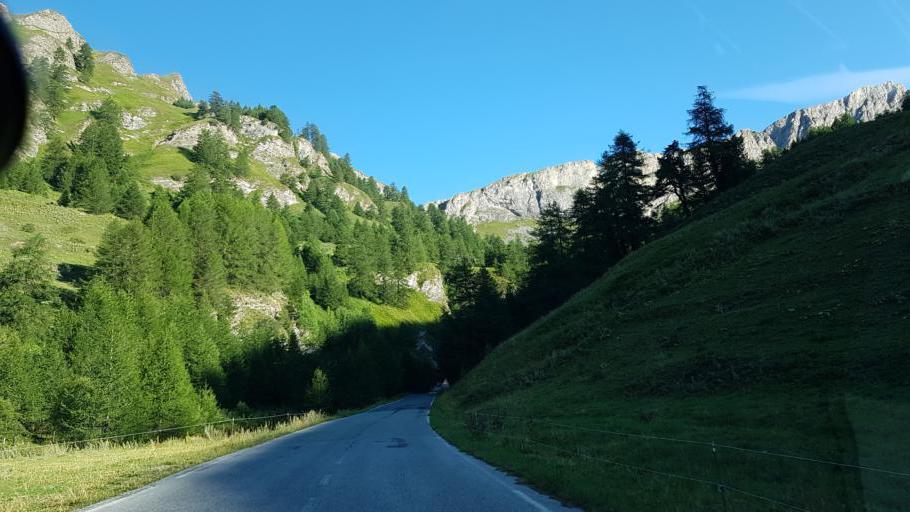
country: IT
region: Piedmont
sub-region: Provincia di Cuneo
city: Pontechianale
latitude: 44.6533
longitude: 6.9918
